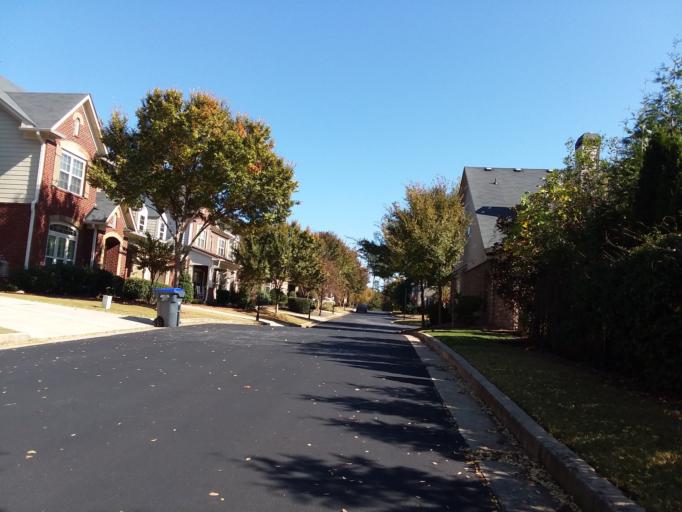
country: US
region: Georgia
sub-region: Fulton County
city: Johns Creek
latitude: 34.0258
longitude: -84.2557
